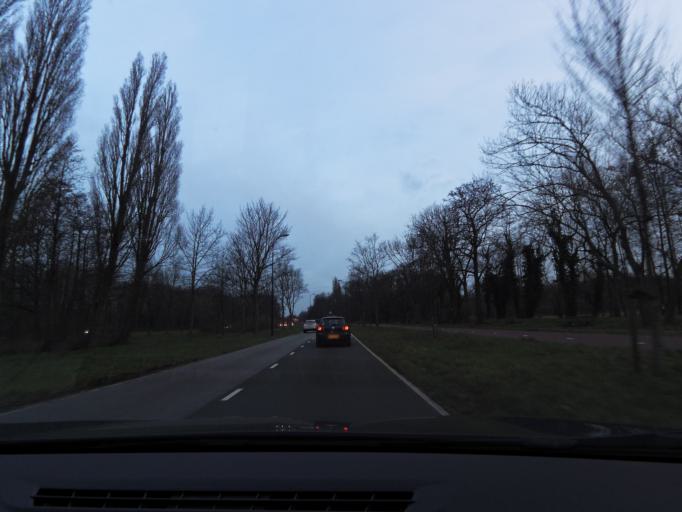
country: NL
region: South Holland
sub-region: Gemeente Rijswijk
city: Rijswijk
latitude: 52.0443
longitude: 4.3071
